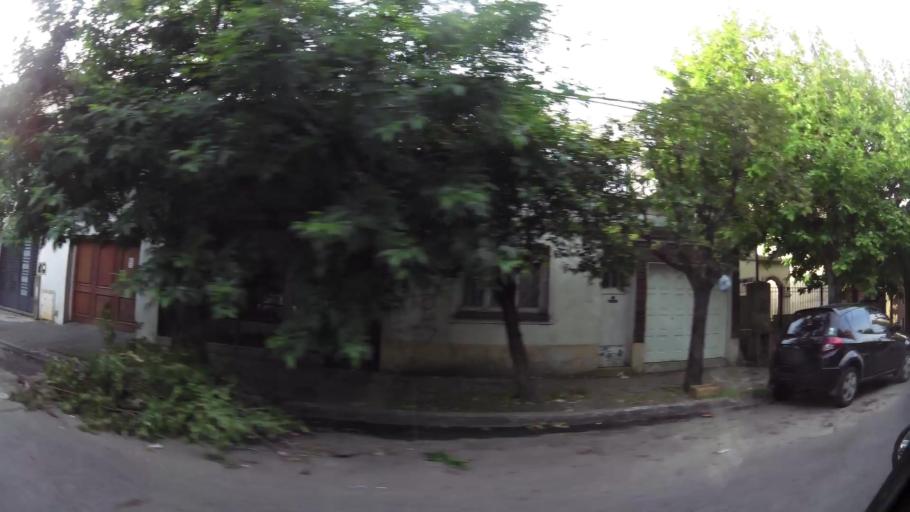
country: AR
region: Buenos Aires
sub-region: Partido de Quilmes
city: Quilmes
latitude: -34.7275
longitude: -58.2489
